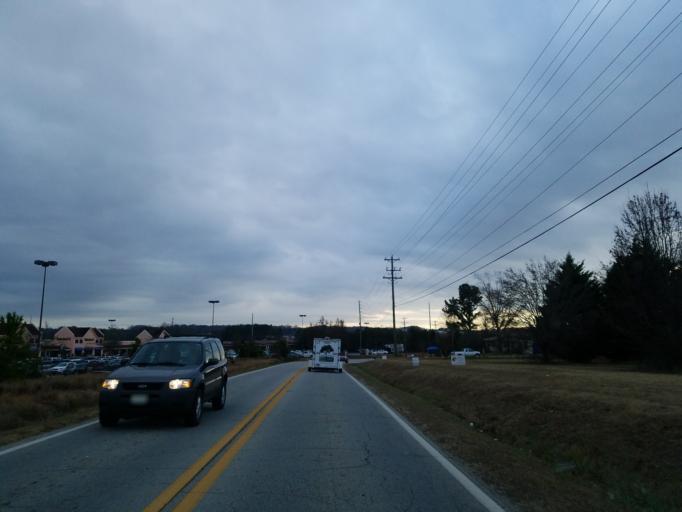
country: US
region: Georgia
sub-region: Dawson County
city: Dawsonville
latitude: 34.3573
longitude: -84.0502
